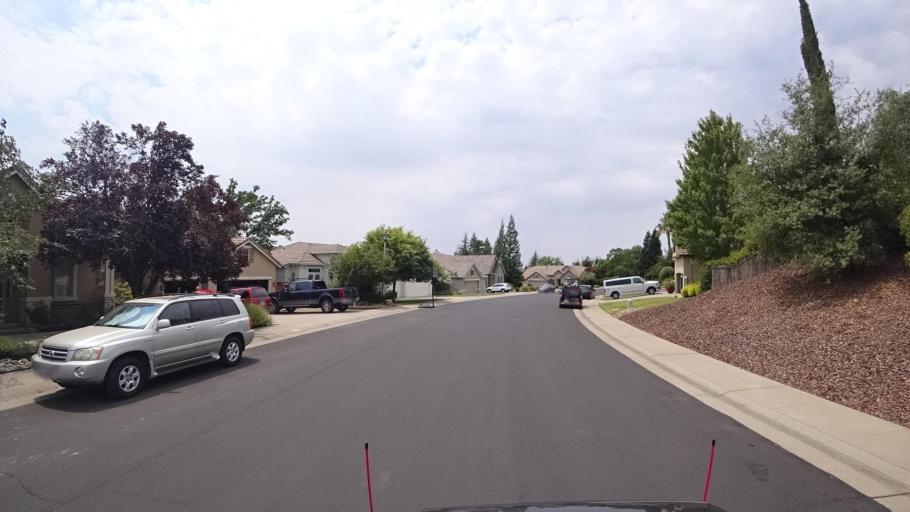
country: US
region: California
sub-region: Placer County
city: Rocklin
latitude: 38.7760
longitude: -121.2169
